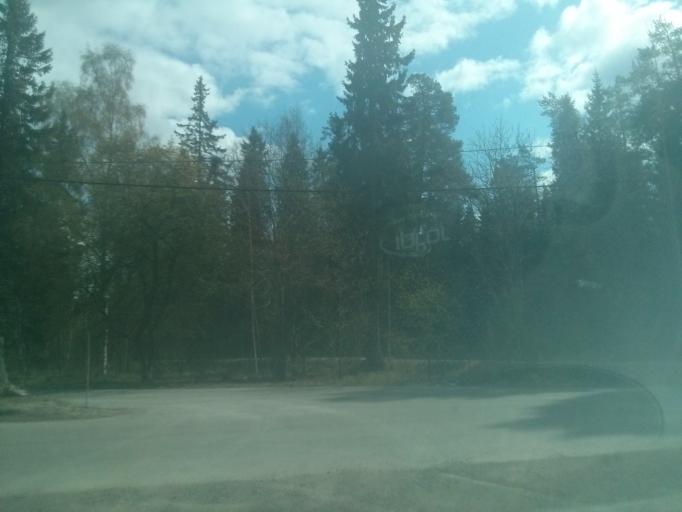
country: SE
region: Vaesternorrland
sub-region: Sundsvalls Kommun
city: Sundsvall
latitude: 62.3994
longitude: 17.3035
